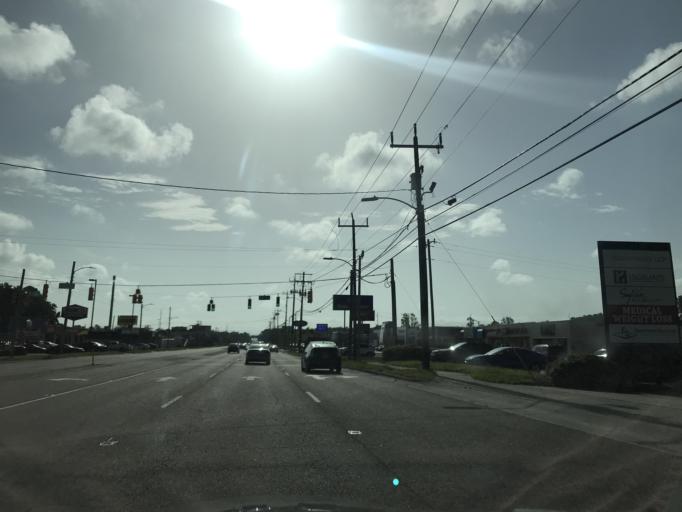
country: US
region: North Carolina
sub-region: New Hanover County
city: Seagate
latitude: 34.2109
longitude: -77.8929
